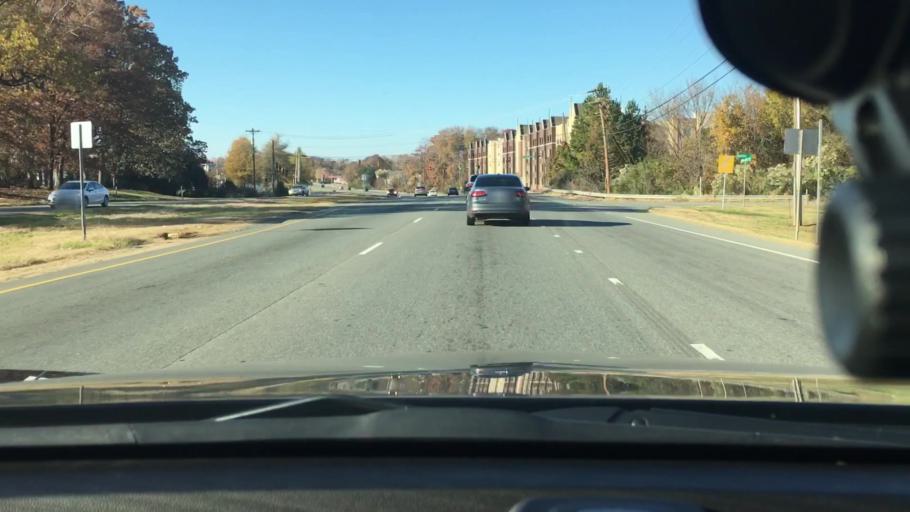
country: US
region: North Carolina
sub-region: Cabarrus County
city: Harrisburg
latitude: 35.3097
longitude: -80.7173
